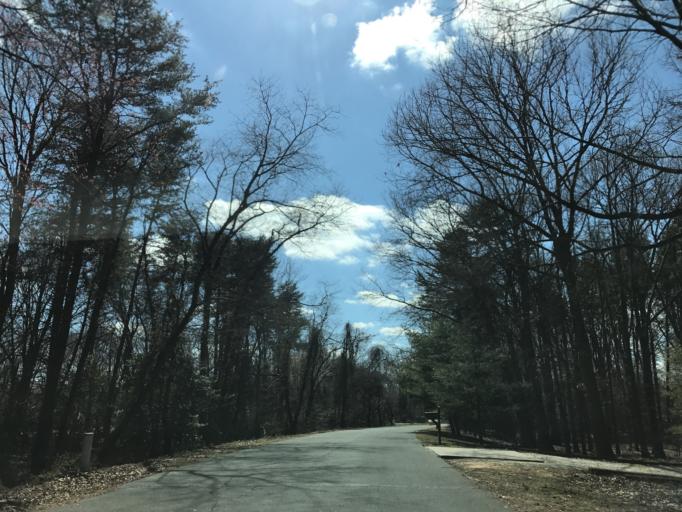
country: US
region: Maryland
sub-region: Anne Arundel County
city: Green Haven
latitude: 39.1139
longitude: -76.5234
